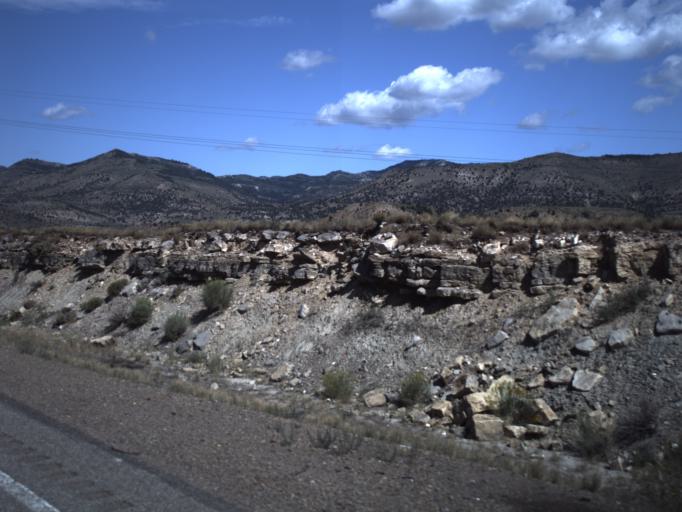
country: US
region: Utah
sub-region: Carbon County
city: Helper
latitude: 39.8229
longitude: -110.9459
